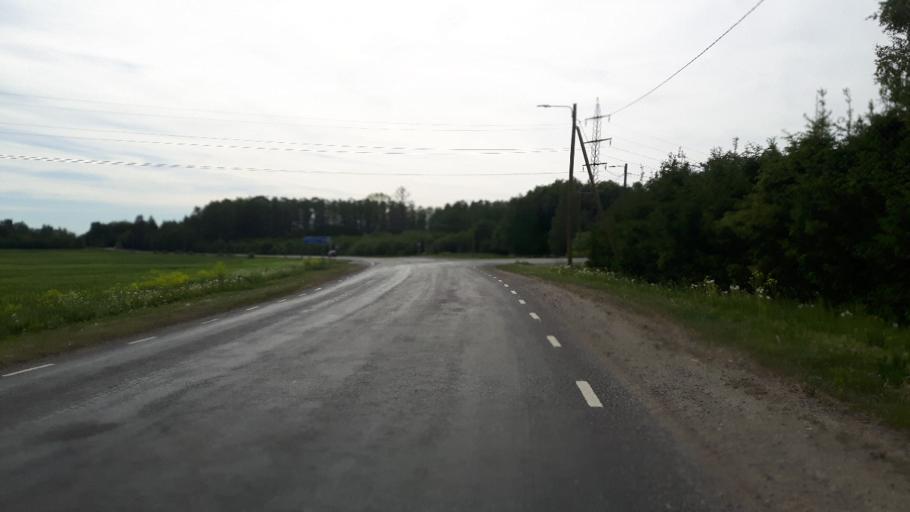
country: EE
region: Harju
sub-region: Maardu linn
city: Maardu
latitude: 59.4258
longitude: 25.0192
